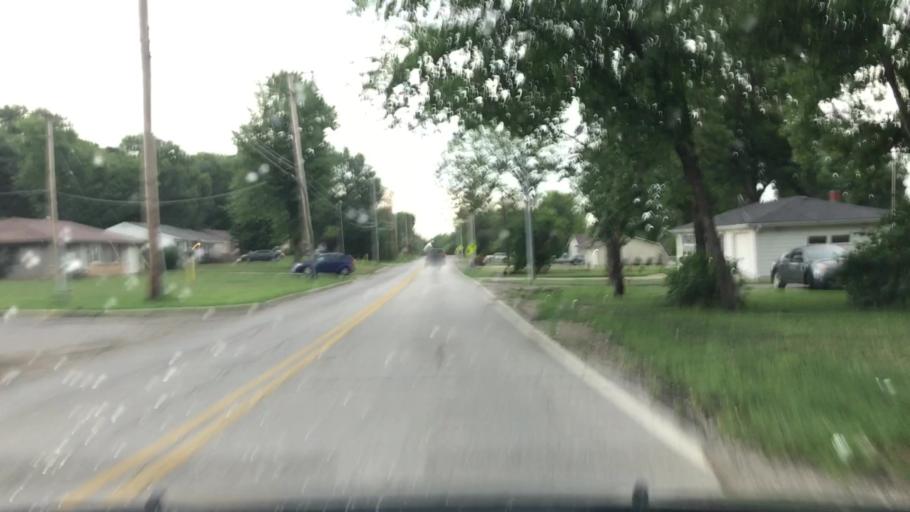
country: US
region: Missouri
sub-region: Jackson County
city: Grandview
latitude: 38.9301
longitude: -94.4955
